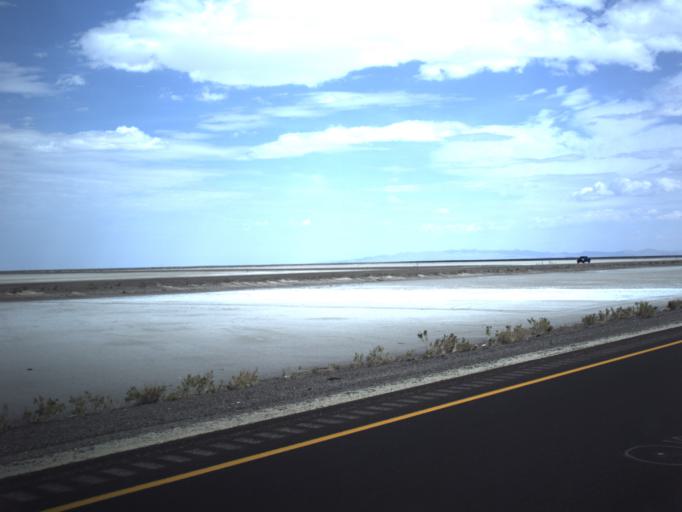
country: US
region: Utah
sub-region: Tooele County
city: Wendover
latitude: 40.7327
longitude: -113.5776
